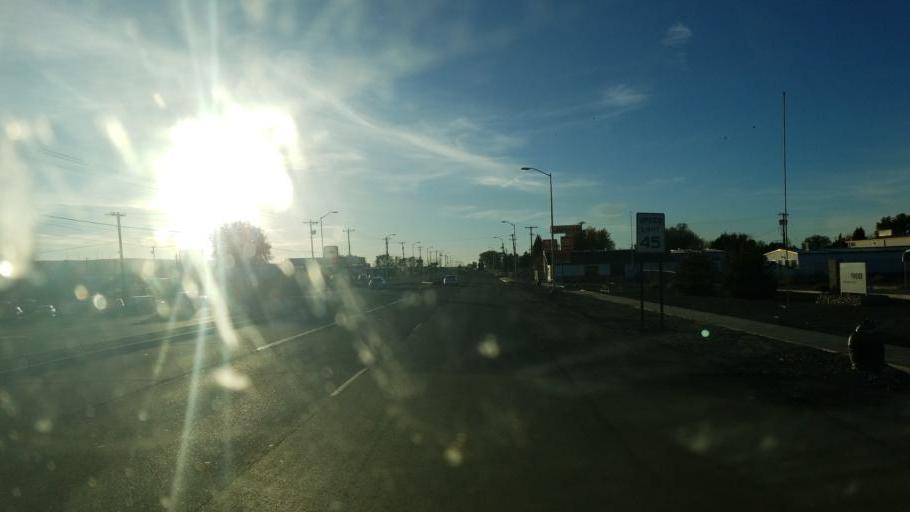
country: US
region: New Mexico
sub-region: San Juan County
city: Farmington
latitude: 36.7194
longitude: -108.1700
